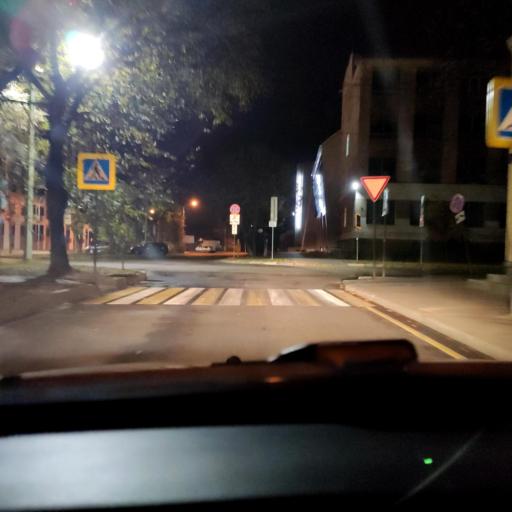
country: RU
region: Voronezj
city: Voronezh
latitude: 51.6538
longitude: 39.1926
